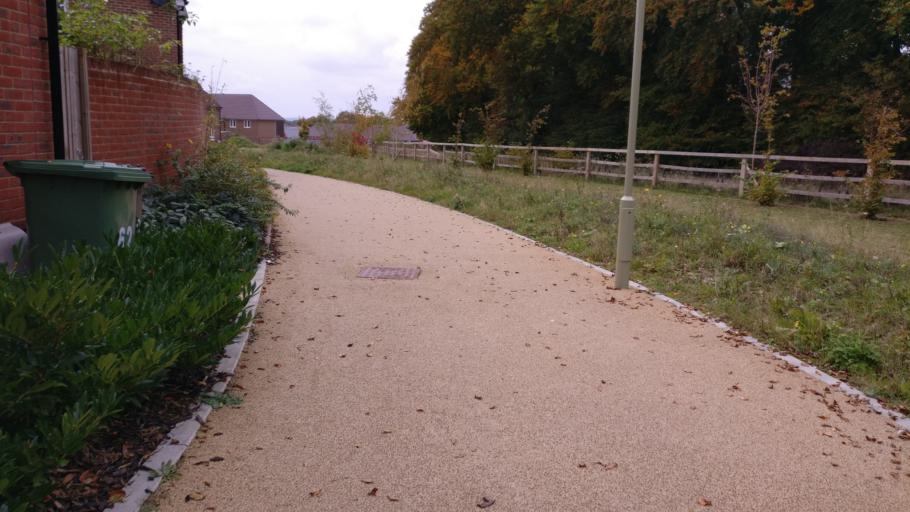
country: GB
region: England
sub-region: Hampshire
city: Basingstoke
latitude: 51.2332
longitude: -1.1459
